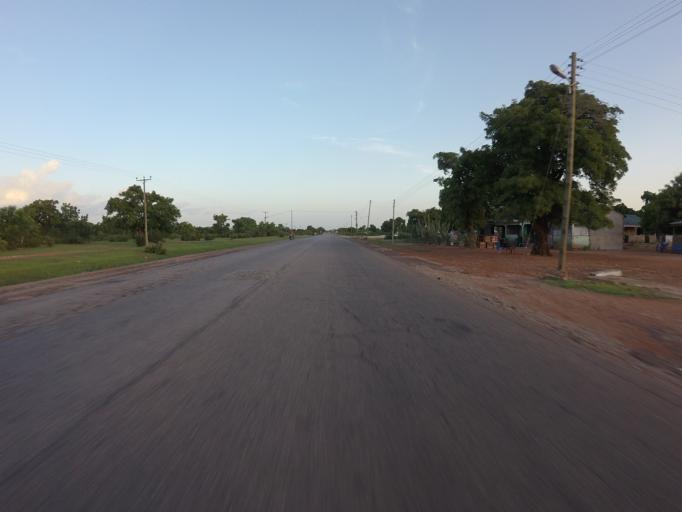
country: GH
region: Upper East
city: Navrongo
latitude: 10.9457
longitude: -1.0936
